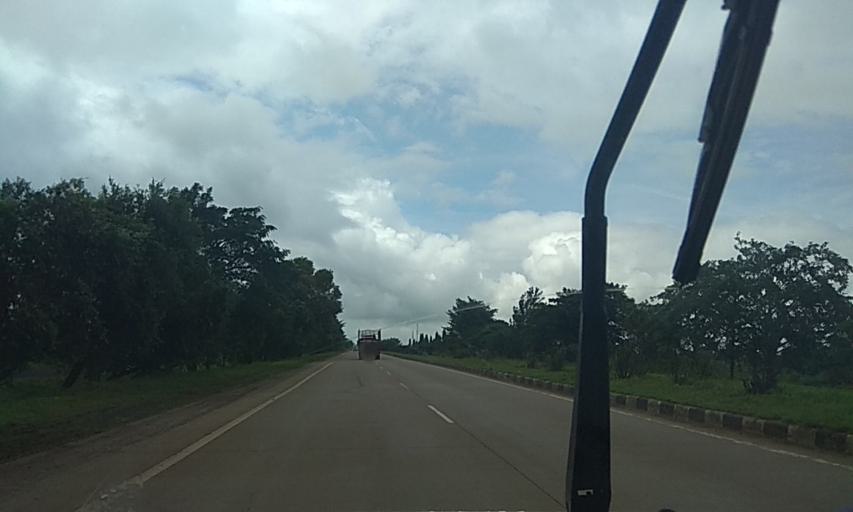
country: IN
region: Karnataka
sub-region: Belgaum
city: Sankeshwar
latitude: 16.2993
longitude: 74.4354
